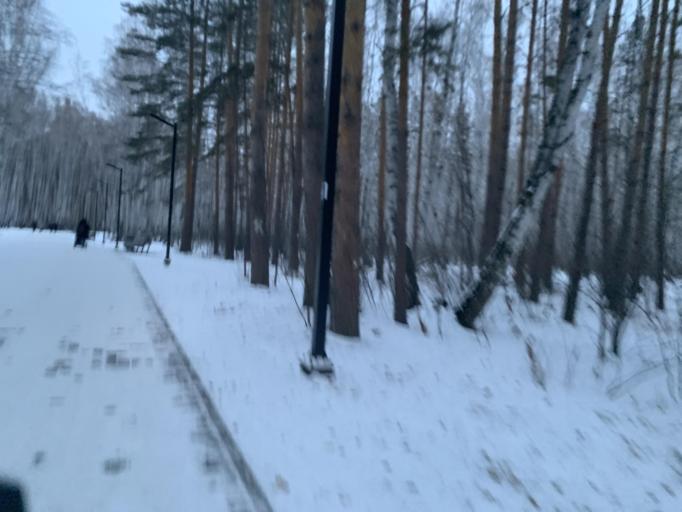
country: RU
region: Chelyabinsk
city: Roshchino
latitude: 55.1956
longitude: 61.2905
